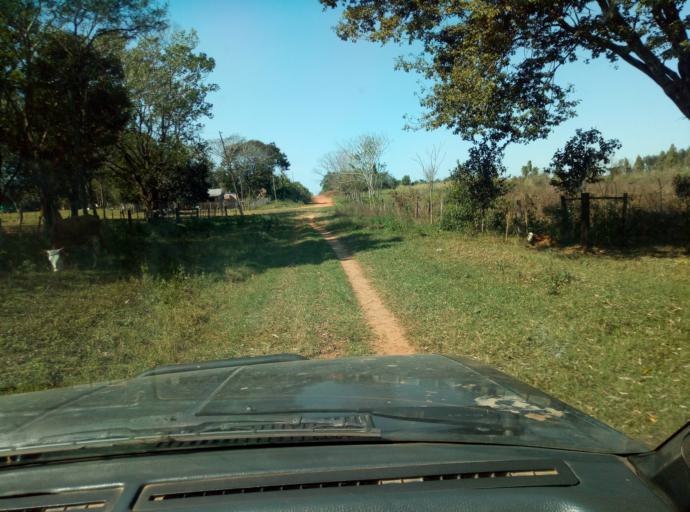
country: PY
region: Caaguazu
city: Doctor Cecilio Baez
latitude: -25.1793
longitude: -56.2128
